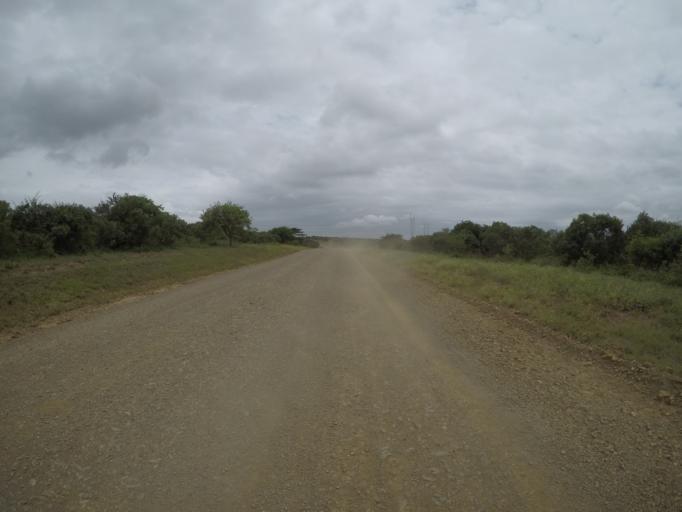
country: ZA
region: KwaZulu-Natal
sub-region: uThungulu District Municipality
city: Empangeni
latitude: -28.5998
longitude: 31.8282
